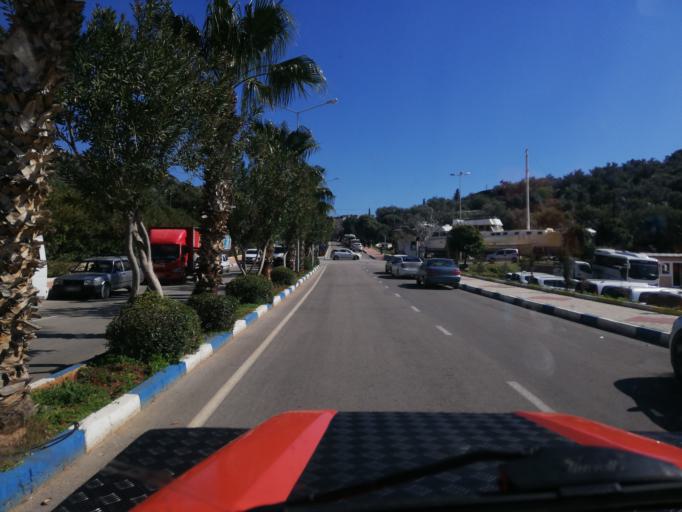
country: TR
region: Antalya
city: Kas
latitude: 36.2030
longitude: 29.6351
